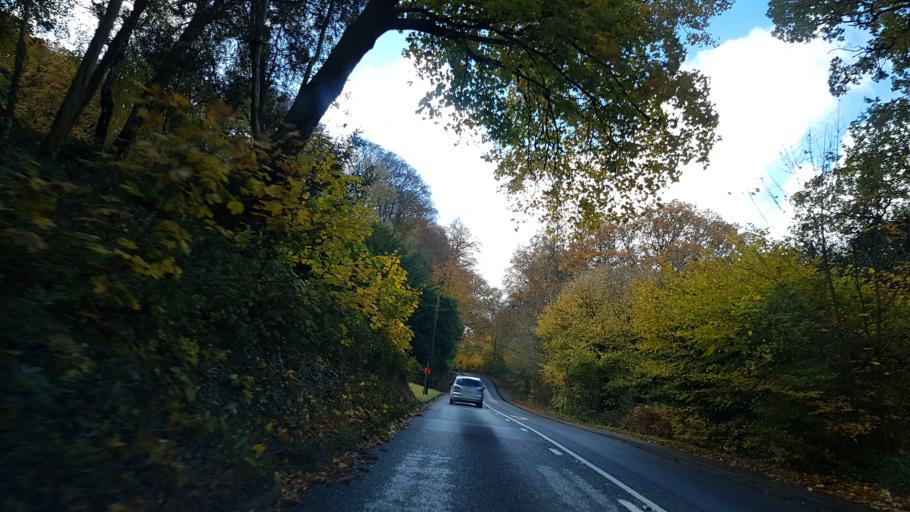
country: GB
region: England
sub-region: Surrey
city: Haslemere
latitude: 51.0990
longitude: -0.6989
